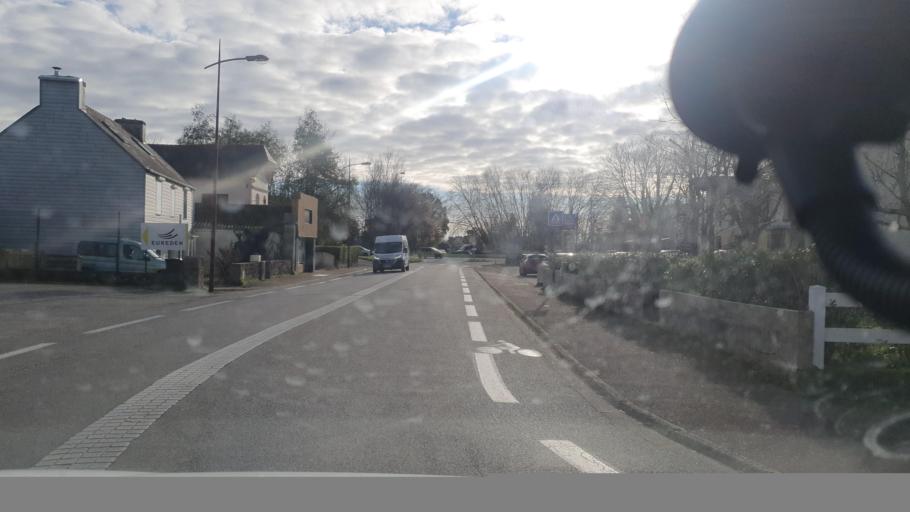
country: FR
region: Brittany
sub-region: Departement du Finistere
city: Briec
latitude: 48.0976
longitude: -4.0013
